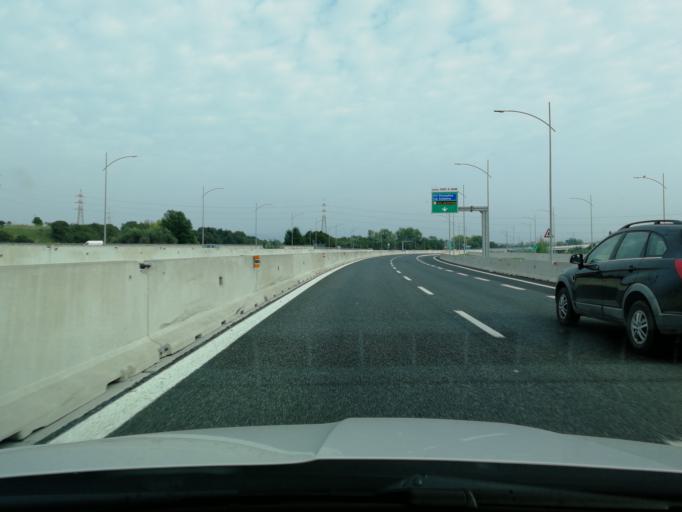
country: IT
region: Latium
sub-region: Citta metropolitana di Roma Capitale
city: Setteville
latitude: 41.9237
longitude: 12.6445
